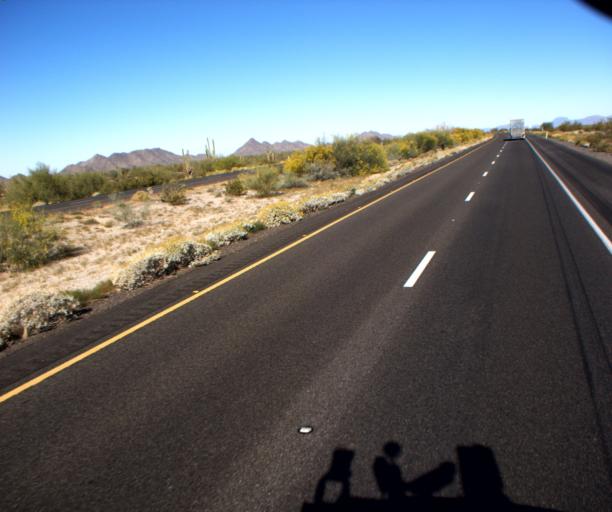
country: US
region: Arizona
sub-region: Maricopa County
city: Gila Bend
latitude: 32.8755
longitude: -112.4461
